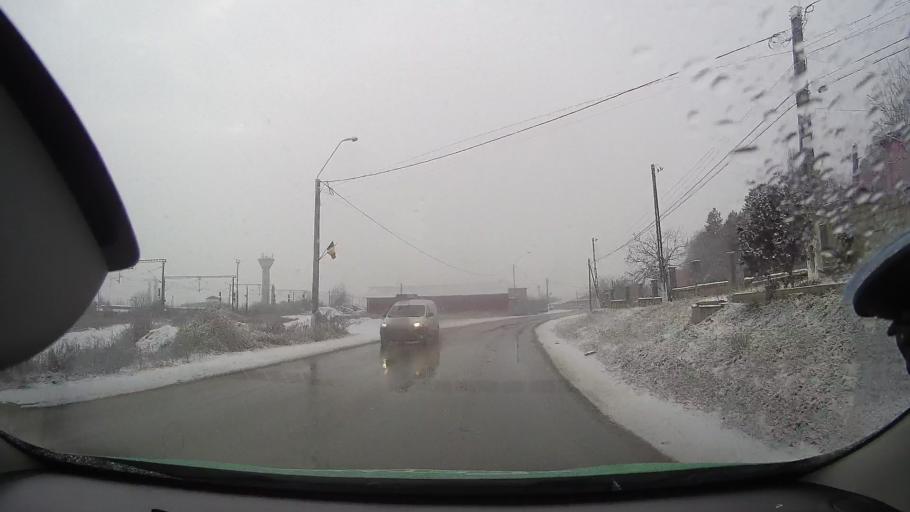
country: RO
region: Alba
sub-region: Municipiul Aiud
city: Aiud
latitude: 46.3089
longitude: 23.7351
